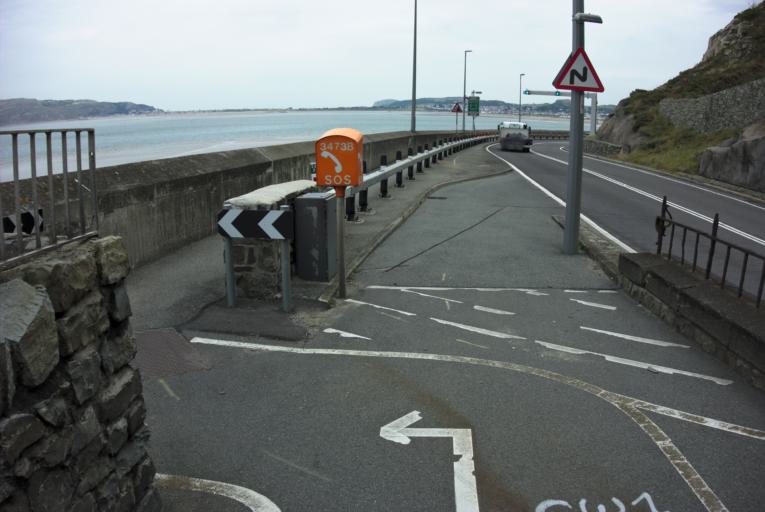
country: GB
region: Wales
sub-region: Conwy
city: Conwy
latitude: 53.2890
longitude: -3.8814
